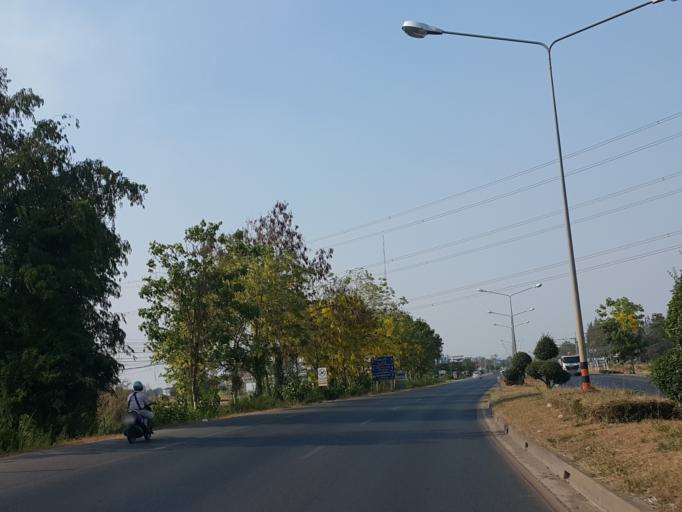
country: TH
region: Phitsanulok
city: Phitsanulok
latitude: 16.8218
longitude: 100.3308
